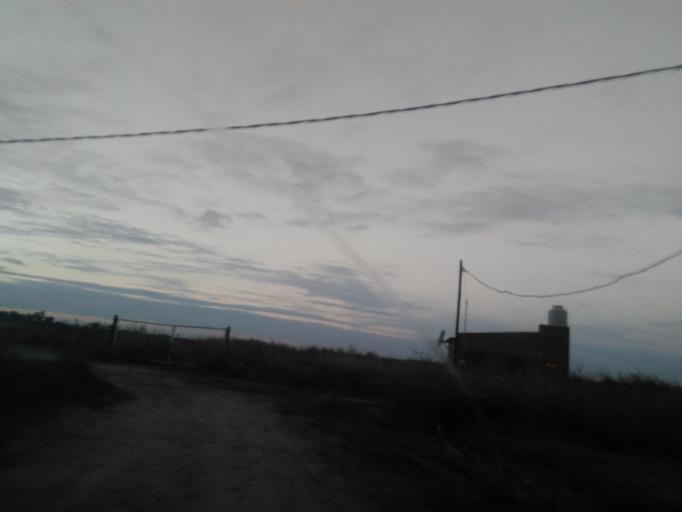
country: AR
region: Chaco
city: Fontana
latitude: -27.3960
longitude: -58.9935
